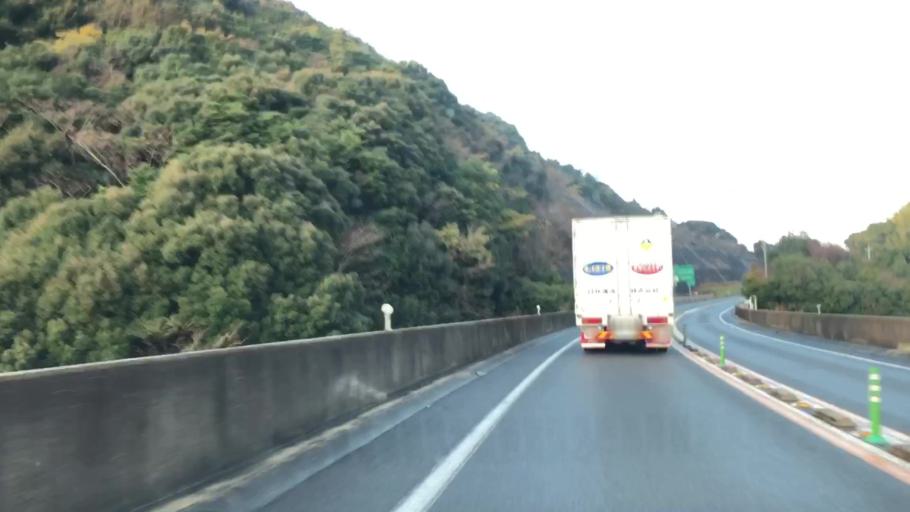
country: JP
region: Nagasaki
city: Sasebo
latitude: 33.1503
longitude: 129.8059
